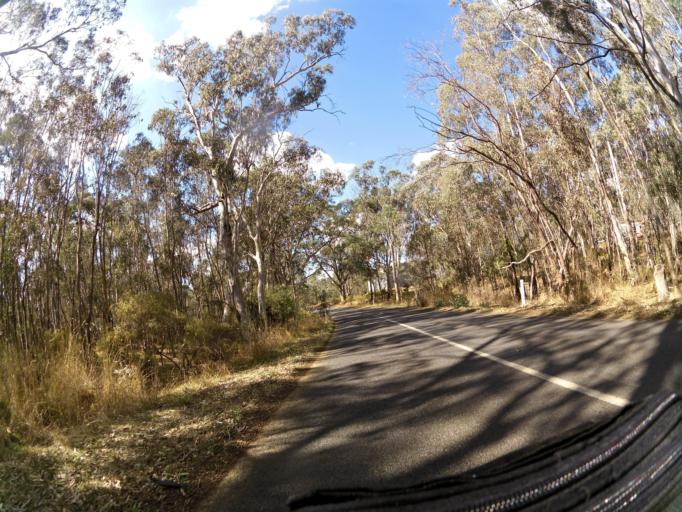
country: AU
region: Victoria
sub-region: Greater Bendigo
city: Kennington
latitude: -36.9544
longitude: 144.7716
